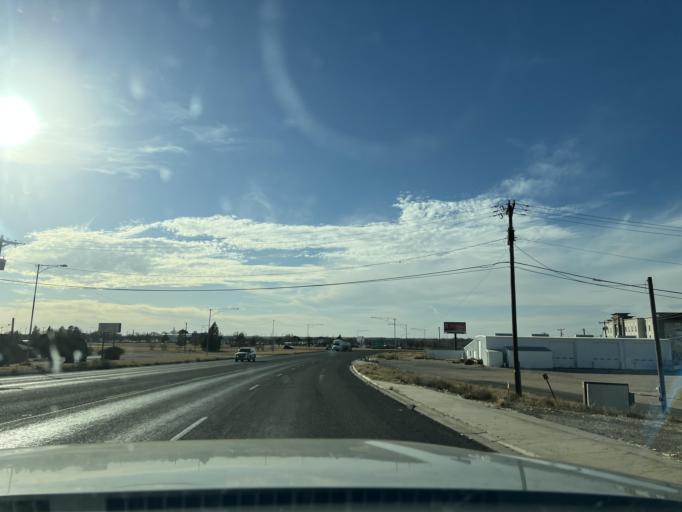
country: US
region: Texas
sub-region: Scurry County
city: Snyder
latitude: 32.7026
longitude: -100.8764
